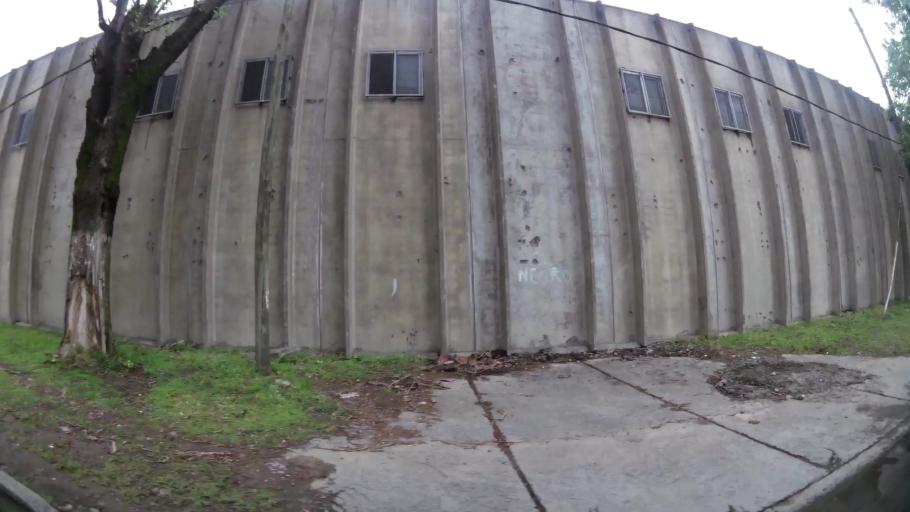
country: AR
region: Buenos Aires
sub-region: Partido de Lanus
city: Lanus
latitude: -34.7095
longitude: -58.3618
